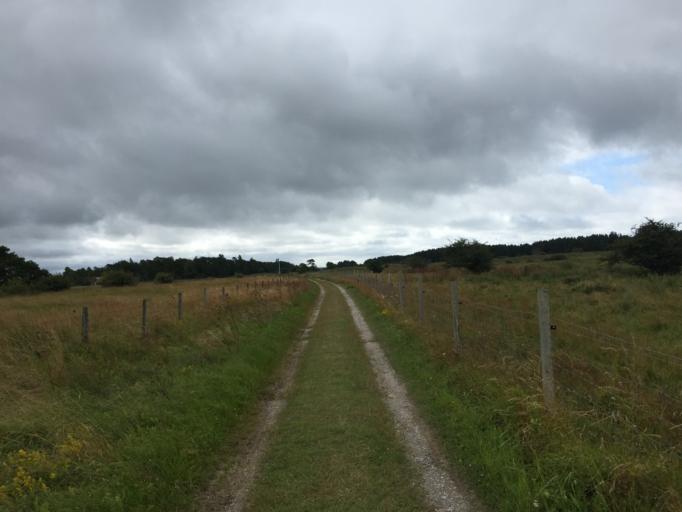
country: SE
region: Gotland
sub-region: Gotland
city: Klintehamn
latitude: 57.4517
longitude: 18.1309
